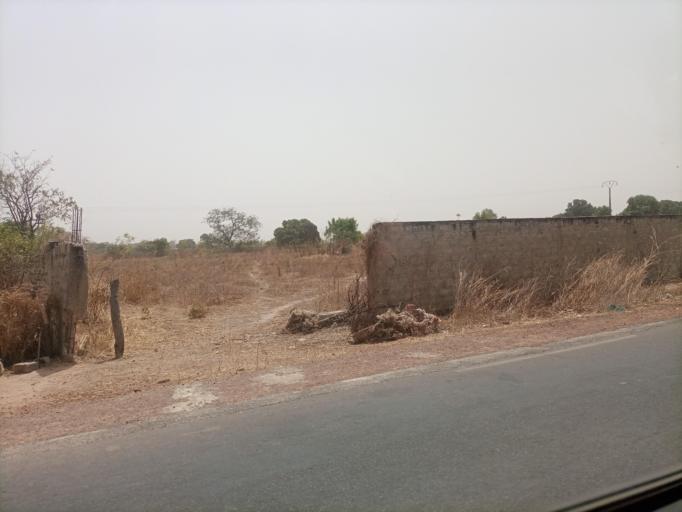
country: SN
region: Fatick
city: Sokone
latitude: 13.7030
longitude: -16.4297
